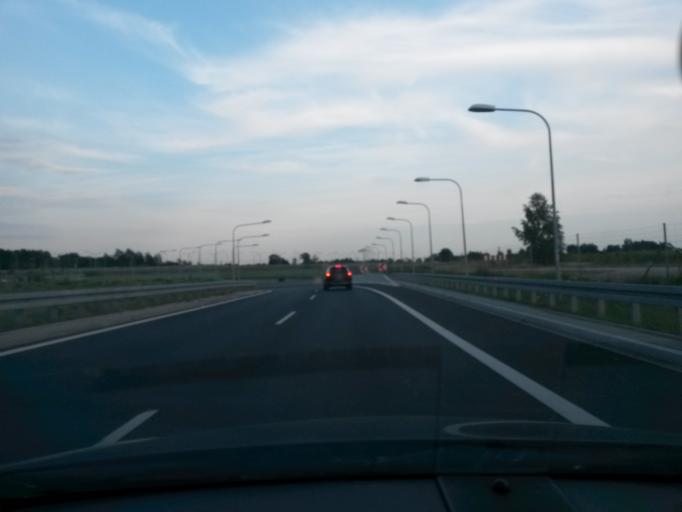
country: PL
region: Masovian Voivodeship
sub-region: Powiat piaseczynski
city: Mysiadlo
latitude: 52.1367
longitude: 20.9863
